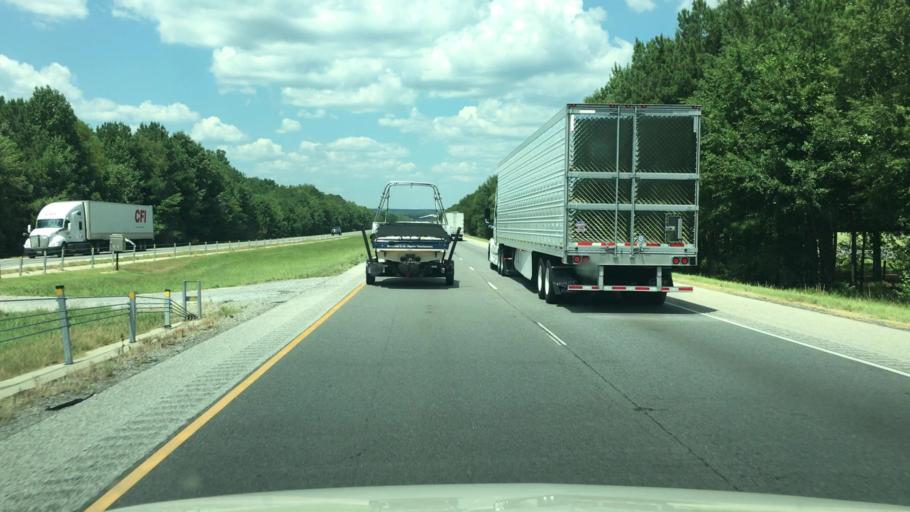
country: US
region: Arkansas
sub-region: Clark County
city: Arkadelphia
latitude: 34.1527
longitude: -93.0781
